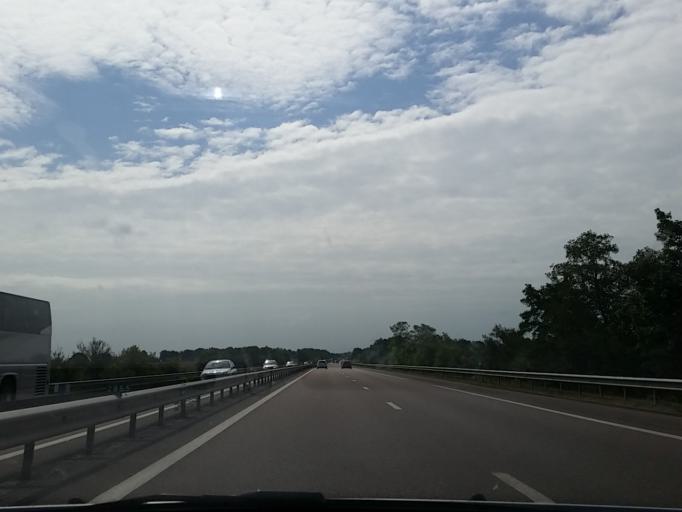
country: FR
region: Auvergne
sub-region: Departement de l'Allier
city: Estivareilles
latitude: 46.4768
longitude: 2.6721
